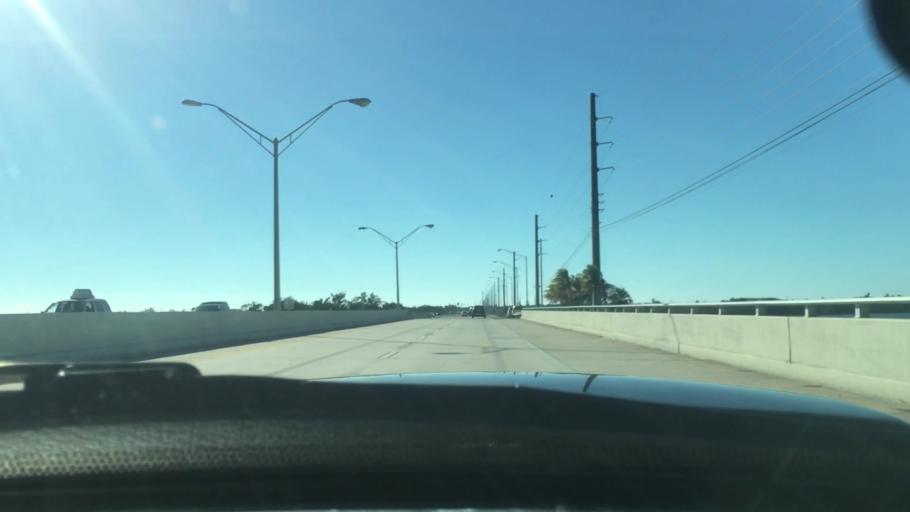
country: US
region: Florida
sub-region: Monroe County
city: Stock Island
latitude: 24.5772
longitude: -81.7199
